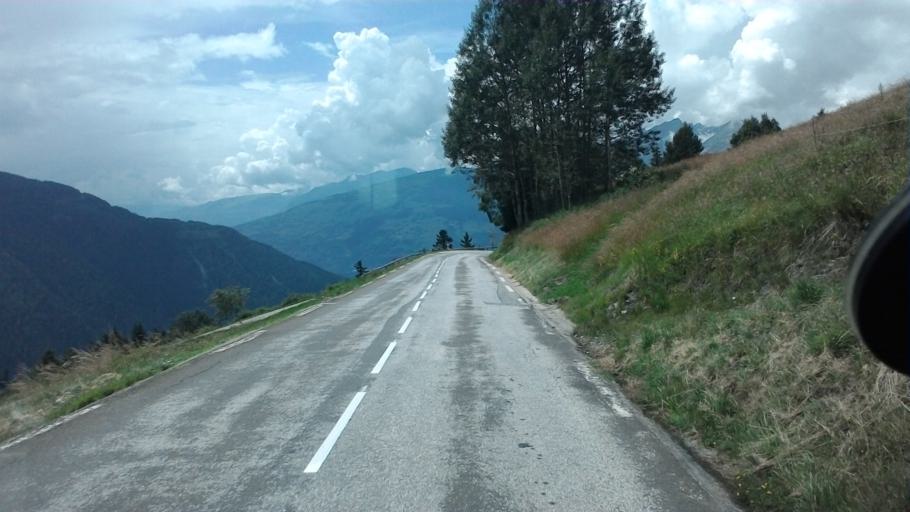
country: FR
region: Rhone-Alpes
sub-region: Departement de la Savoie
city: Seez
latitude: 45.6218
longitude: 6.8477
